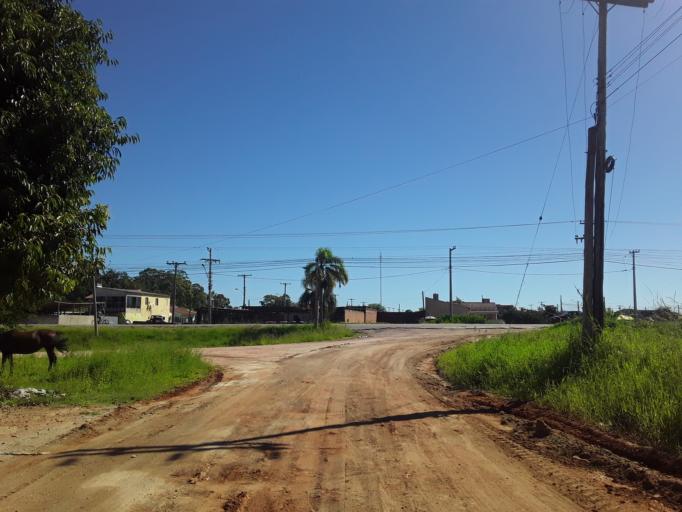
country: BR
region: Rio Grande do Sul
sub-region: Sao Lourenco Do Sul
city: Sao Lourenco do Sul
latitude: -31.3443
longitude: -51.9957
